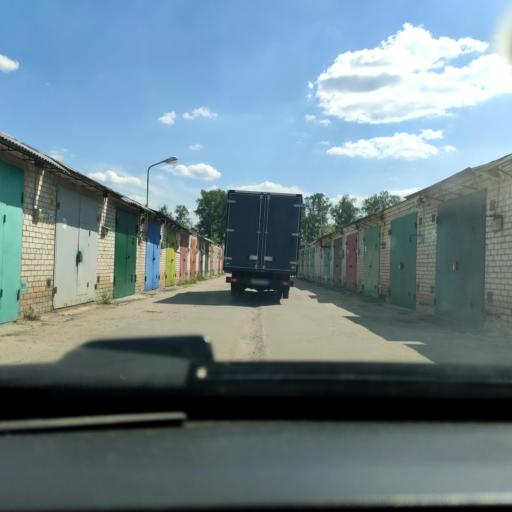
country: RU
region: Voronezj
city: Somovo
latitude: 51.7360
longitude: 39.3042
